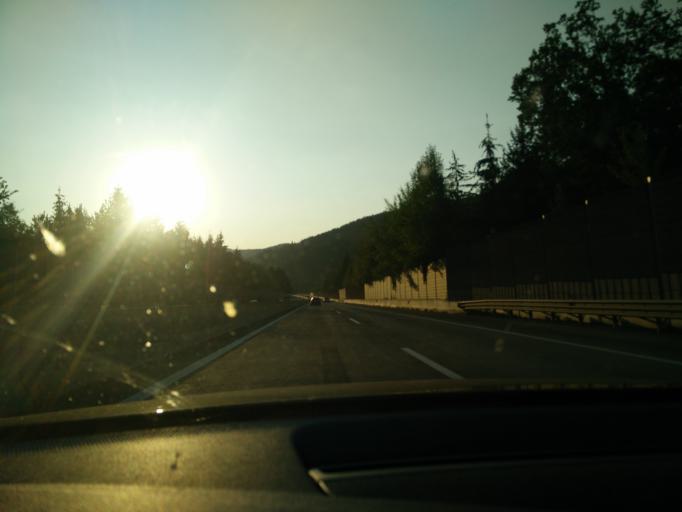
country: AT
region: Carinthia
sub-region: Politischer Bezirk Klagenfurt Land
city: Maria Worth
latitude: 46.6363
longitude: 14.1617
